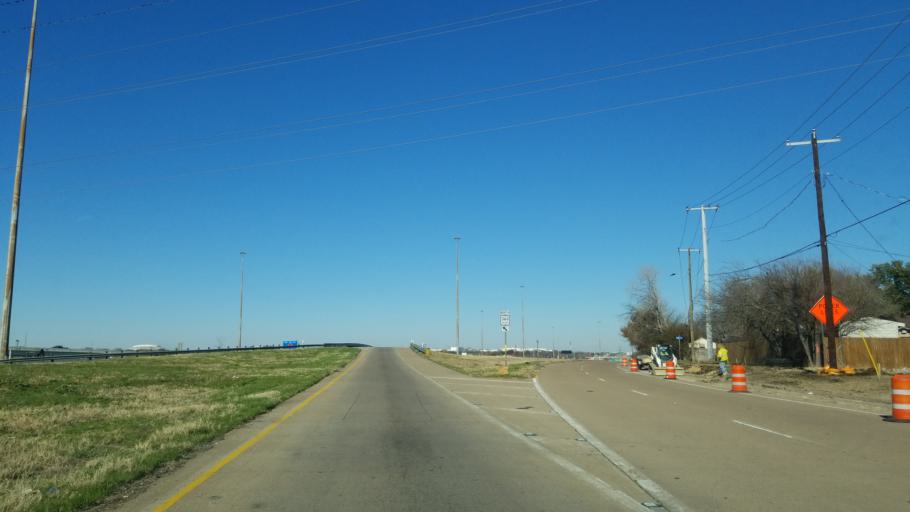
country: US
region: Texas
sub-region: Tarrant County
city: Arlington
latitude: 32.7144
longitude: -97.0615
